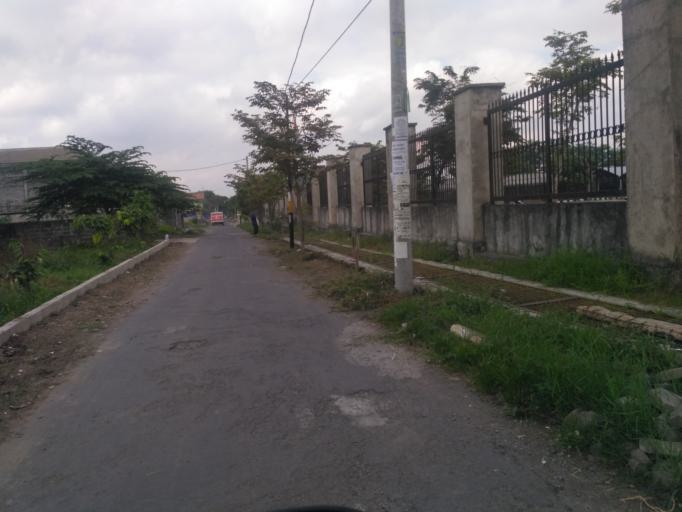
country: ID
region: Daerah Istimewa Yogyakarta
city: Melati
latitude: -7.7488
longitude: 110.3559
